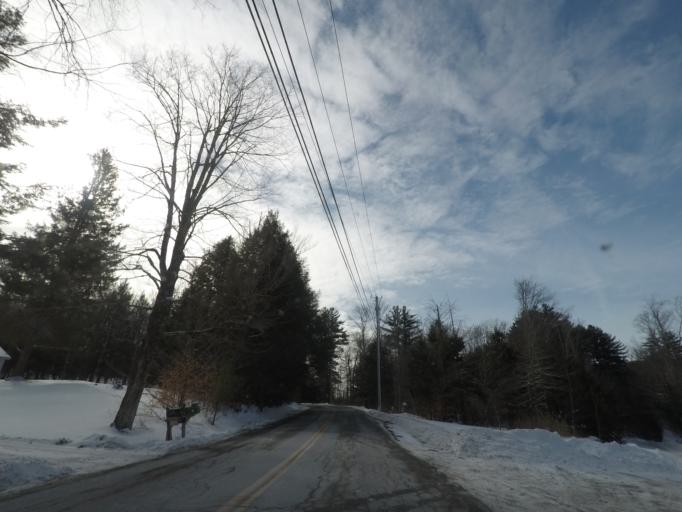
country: US
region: New York
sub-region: Rensselaer County
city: Averill Park
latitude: 42.5803
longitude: -73.4899
